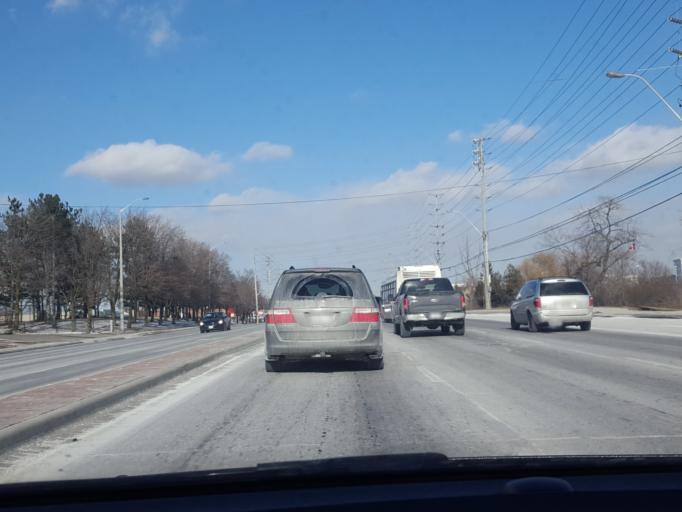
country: CA
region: Ontario
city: Brampton
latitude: 43.6614
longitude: -79.7382
